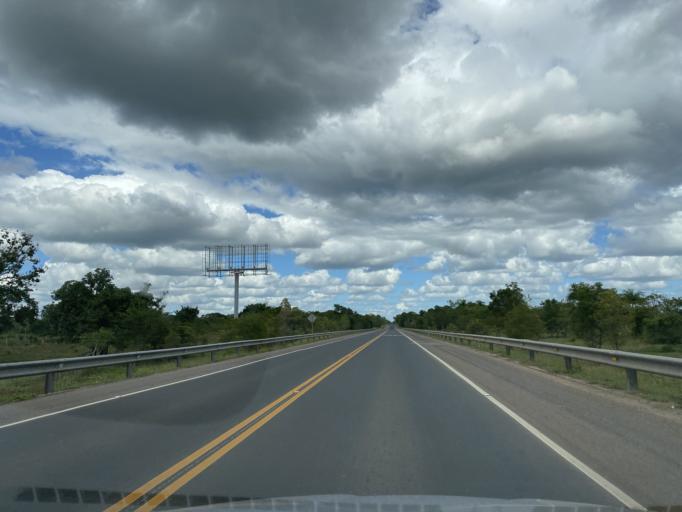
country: DO
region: Santo Domingo
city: Guerra
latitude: 18.6197
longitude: -69.7648
